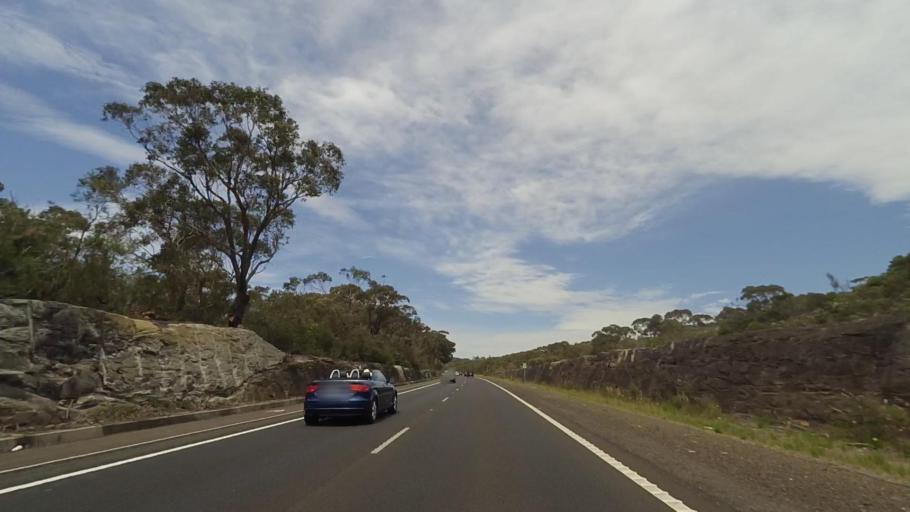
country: AU
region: New South Wales
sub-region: Wollongong
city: Helensburgh
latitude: -34.2305
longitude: 150.9476
